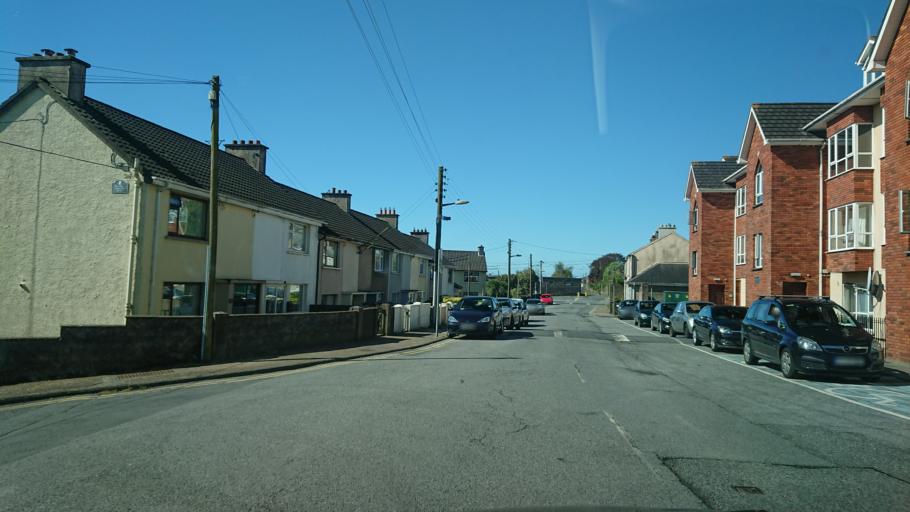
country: IE
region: Munster
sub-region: Waterford
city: Waterford
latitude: 52.2562
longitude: -7.1155
